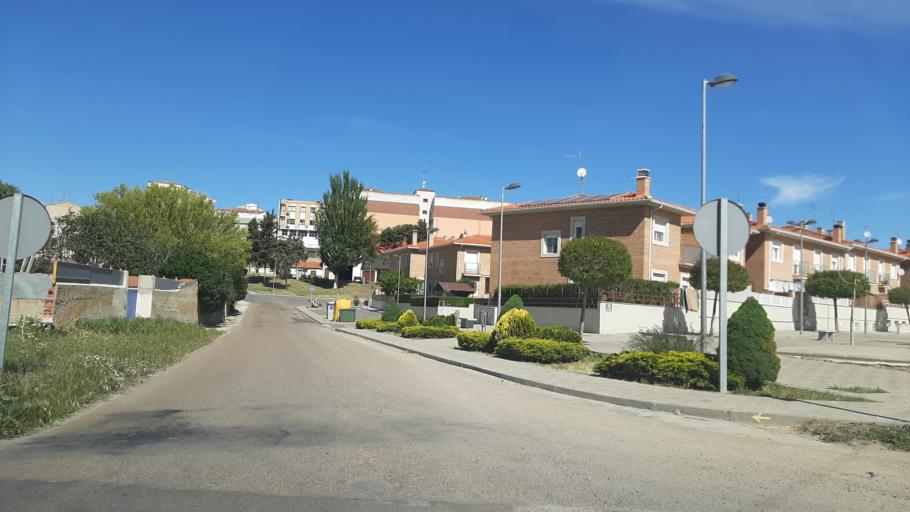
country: ES
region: Castille and Leon
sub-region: Provincia de Salamanca
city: Alba de Tormes
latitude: 40.8237
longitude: -5.5076
